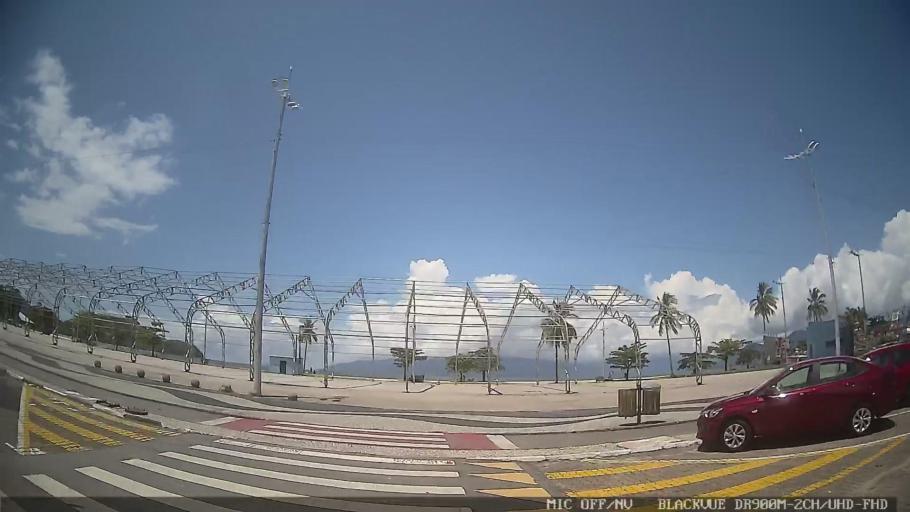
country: BR
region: Sao Paulo
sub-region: Caraguatatuba
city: Caraguatatuba
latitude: -23.6242
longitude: -45.4099
